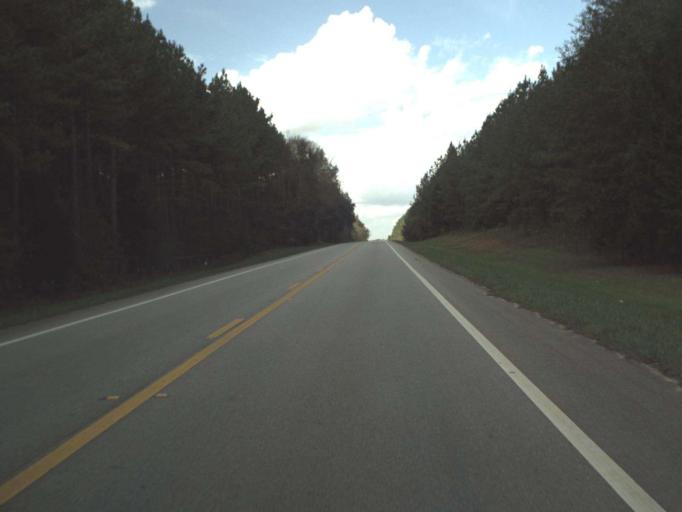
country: US
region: Florida
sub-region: Jackson County
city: Marianna
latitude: 30.8288
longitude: -85.3330
